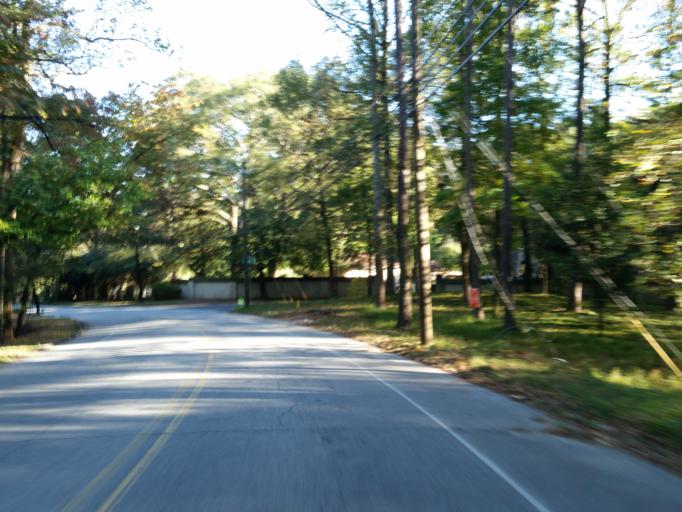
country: US
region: Georgia
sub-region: Cobb County
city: Vinings
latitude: 33.8501
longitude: -84.4362
